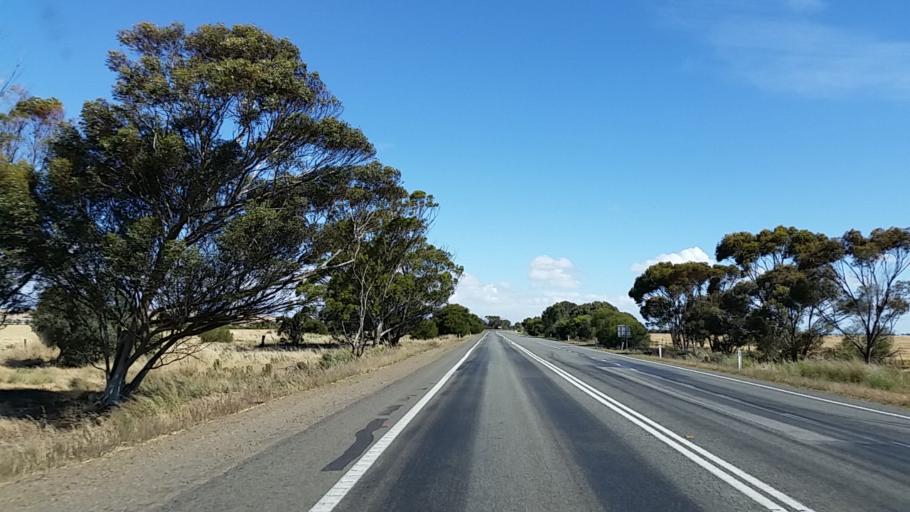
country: AU
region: South Australia
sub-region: Port Pirie City and Dists
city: Crystal Brook
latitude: -33.7587
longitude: 138.2112
